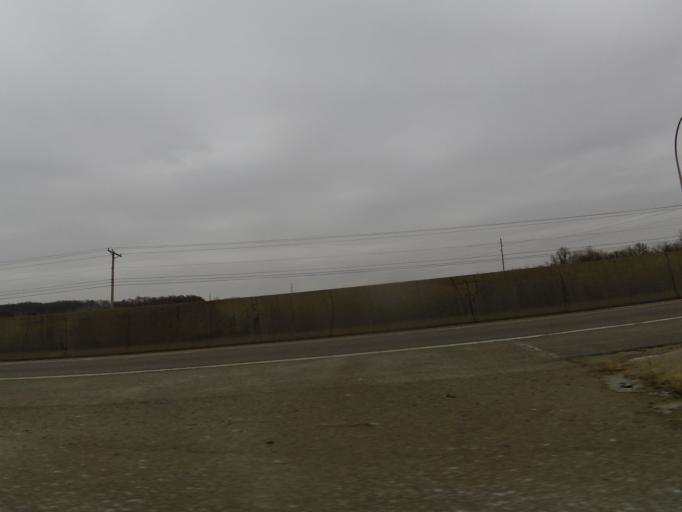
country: US
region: Minnesota
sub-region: Hennepin County
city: Orono
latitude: 44.9948
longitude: -93.6230
